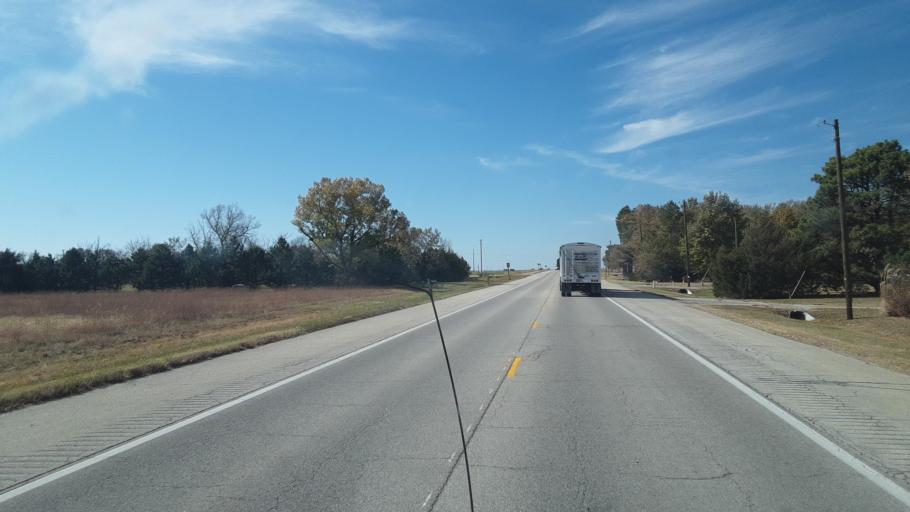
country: US
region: Kansas
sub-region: McPherson County
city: McPherson
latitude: 38.3695
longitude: -97.7012
